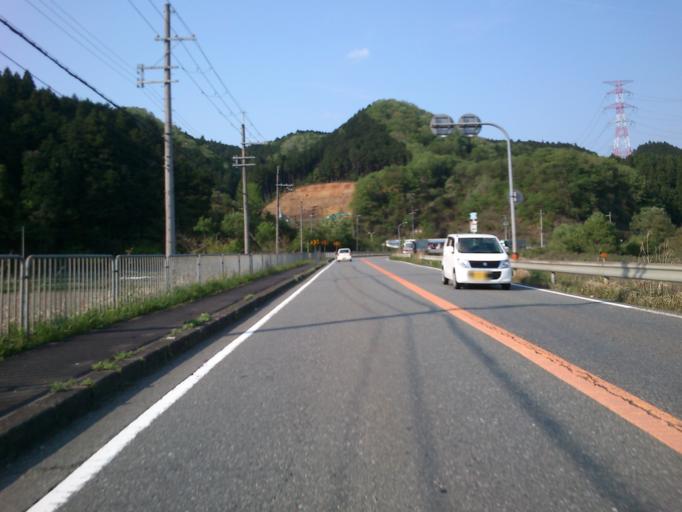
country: JP
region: Kyoto
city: Fukuchiyama
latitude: 35.3243
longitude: 135.0322
